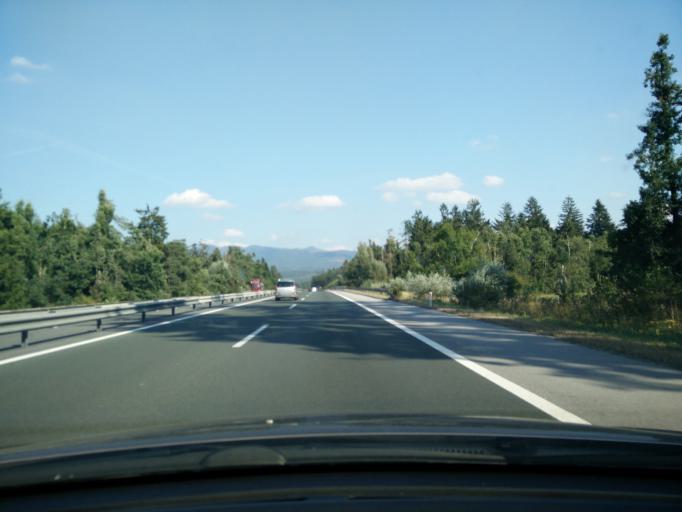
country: SI
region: Postojna
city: Postojna
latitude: 45.7604
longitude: 14.1643
